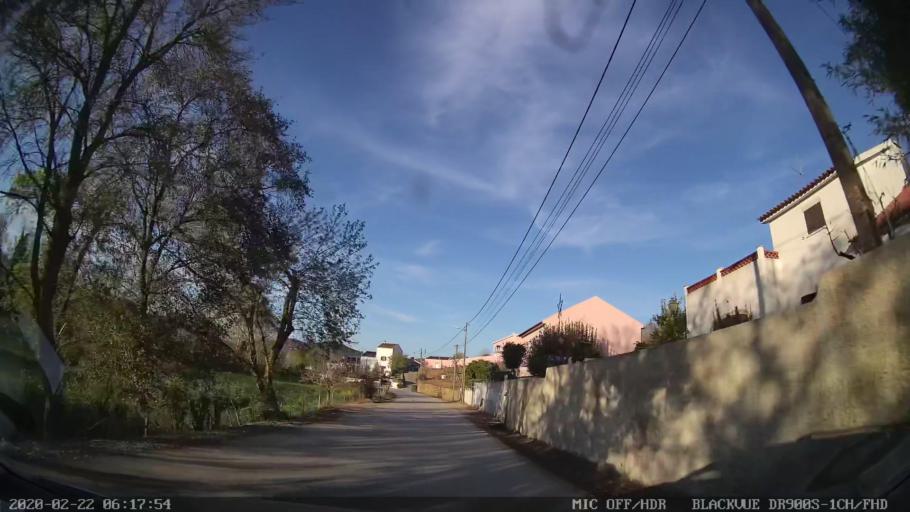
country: PT
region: Lisbon
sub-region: Vila Franca de Xira
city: Castanheira do Ribatejo
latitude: 38.9979
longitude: -9.0073
